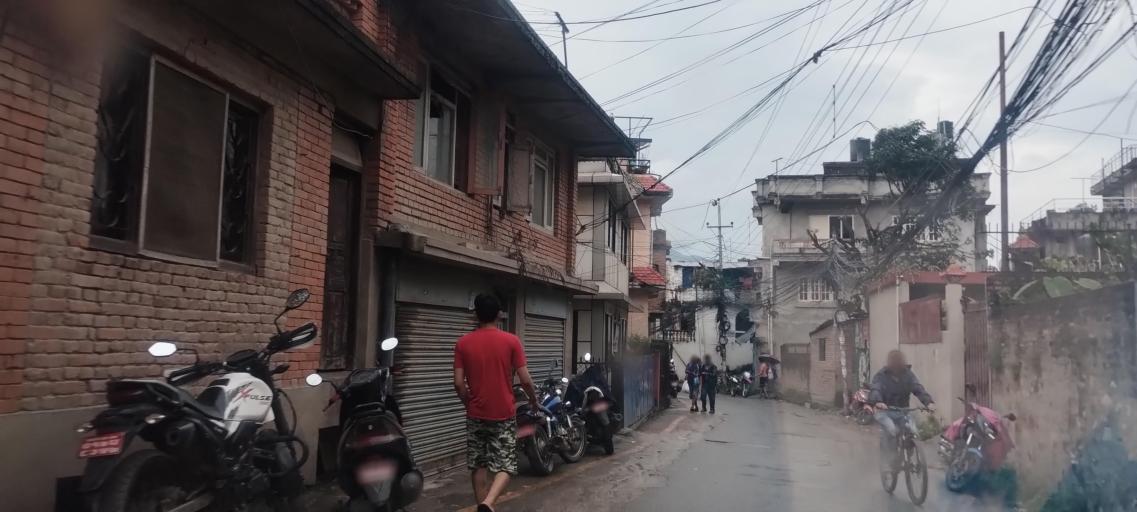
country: NP
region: Central Region
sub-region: Bagmati Zone
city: Kathmandu
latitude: 27.7100
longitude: 85.3396
